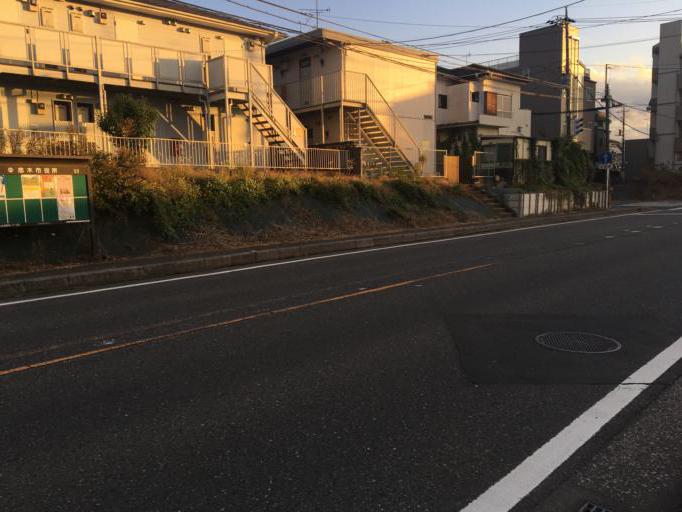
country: JP
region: Saitama
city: Shiki
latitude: 35.8298
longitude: 139.5747
